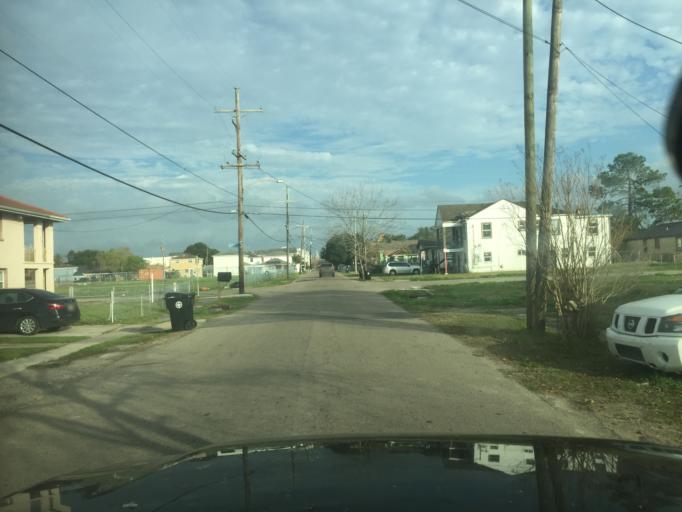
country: US
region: Louisiana
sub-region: Orleans Parish
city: New Orleans
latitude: 29.9946
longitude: -90.0810
